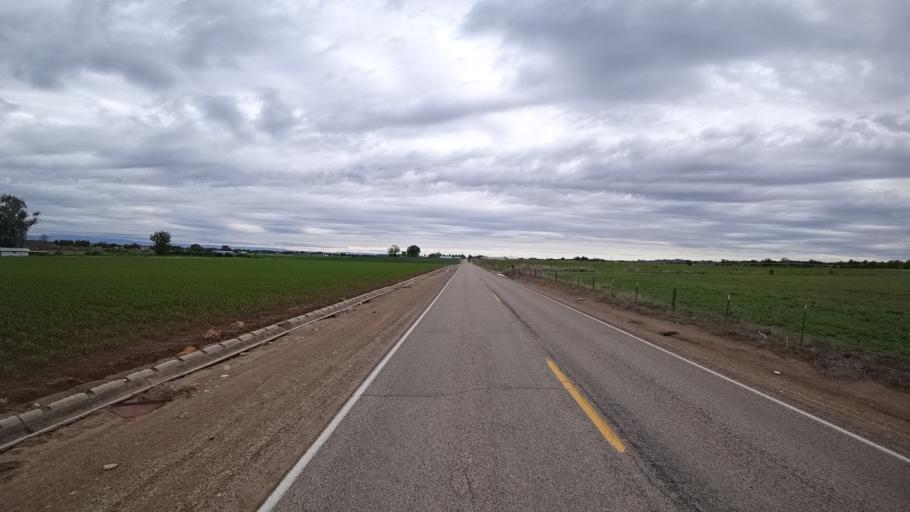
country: US
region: Idaho
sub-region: Ada County
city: Star
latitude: 43.7101
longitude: -116.4476
